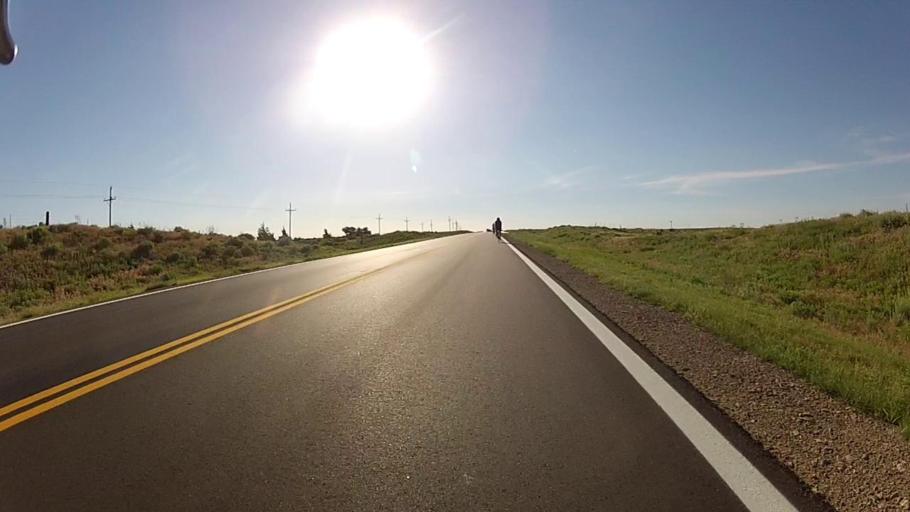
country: US
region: Kansas
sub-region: Comanche County
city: Coldwater
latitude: 37.2804
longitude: -99.0187
